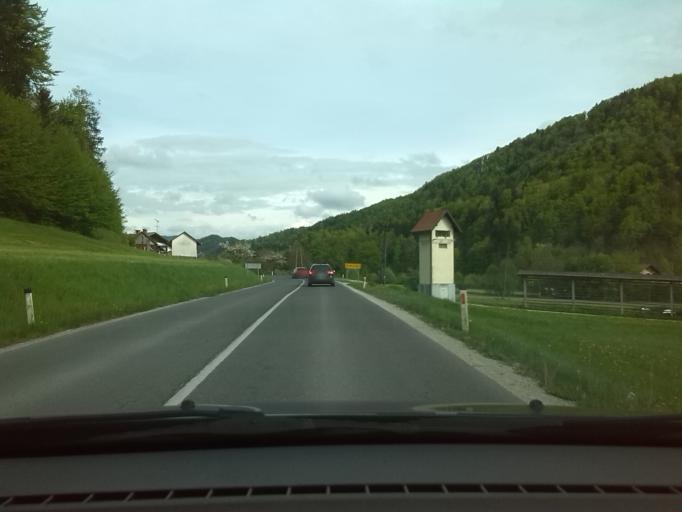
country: SI
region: Kamnik
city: Mekinje
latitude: 46.2264
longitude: 14.6702
